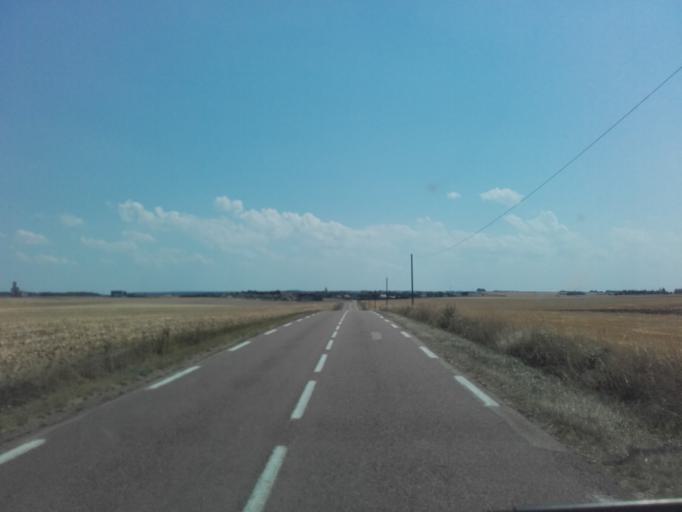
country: FR
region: Bourgogne
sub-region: Departement de l'Yonne
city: Joux-la-Ville
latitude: 47.6876
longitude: 3.8674
